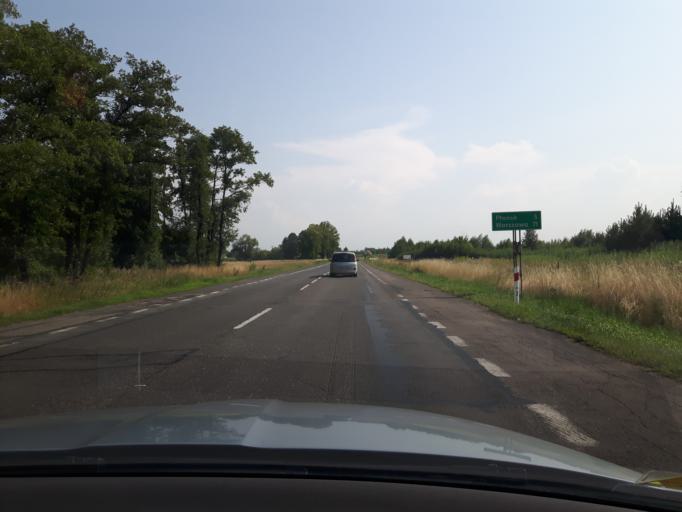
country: PL
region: Masovian Voivodeship
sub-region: Powiat plonski
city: Plonsk
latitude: 52.6654
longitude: 20.3743
